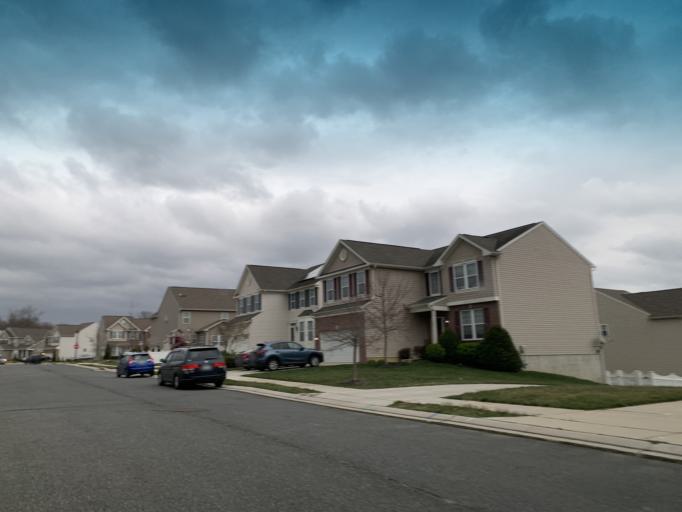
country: US
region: Maryland
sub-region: Harford County
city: Perryman
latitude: 39.4947
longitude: -76.2069
